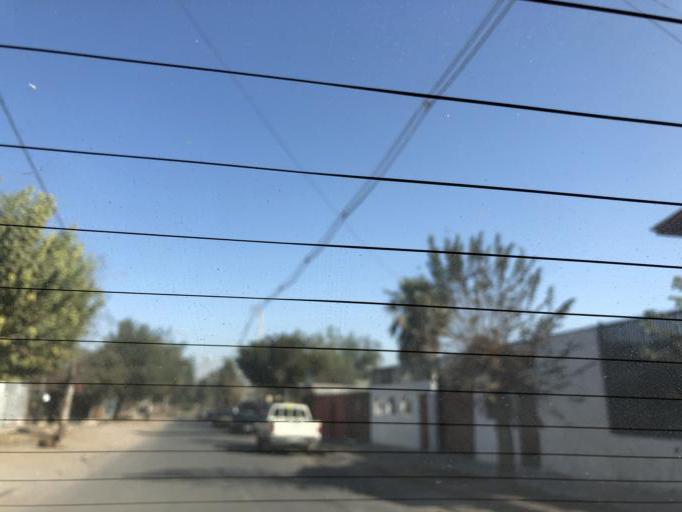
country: CL
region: Santiago Metropolitan
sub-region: Provincia de Santiago
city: La Pintana
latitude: -33.6168
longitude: -70.6253
